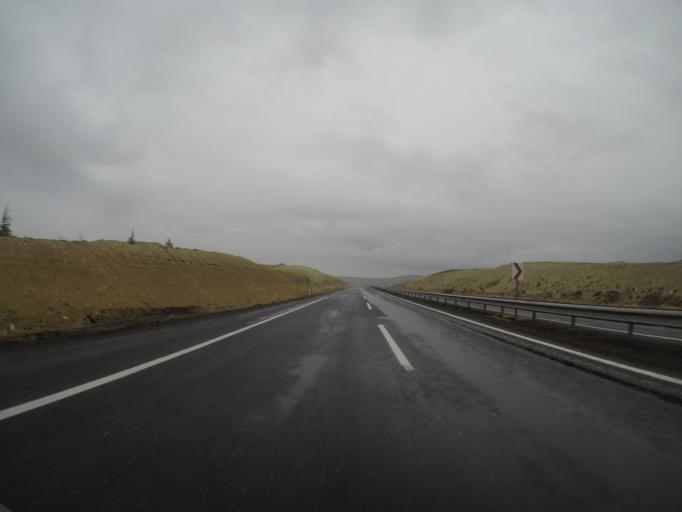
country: TR
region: Nevsehir
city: Avanos
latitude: 38.7100
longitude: 34.8926
